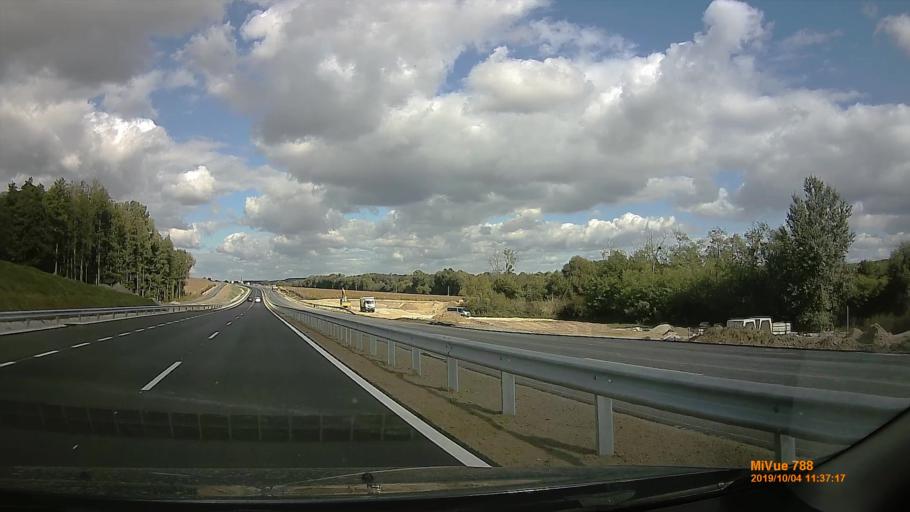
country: HU
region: Somogy
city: Karad
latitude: 46.5342
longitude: 17.8170
